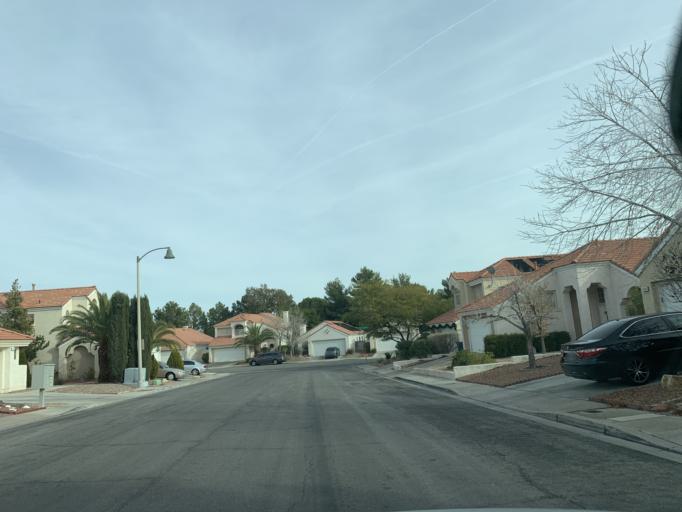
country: US
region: Nevada
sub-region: Clark County
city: Summerlin South
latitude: 36.1354
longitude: -115.3076
